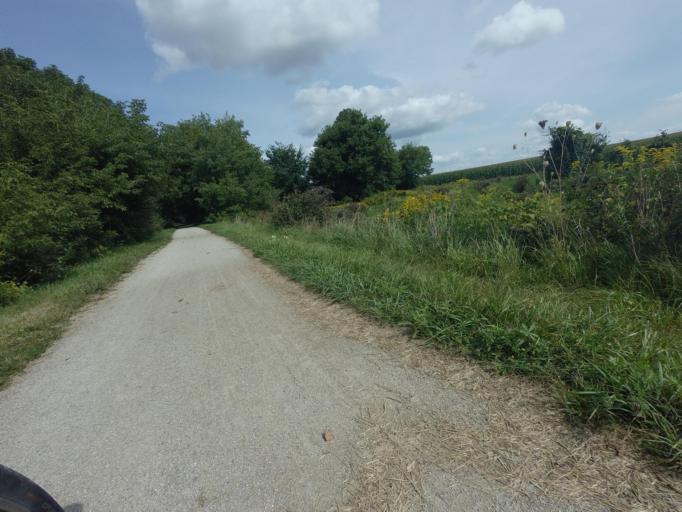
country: CA
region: Ontario
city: Waterloo
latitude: 43.6039
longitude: -80.6280
